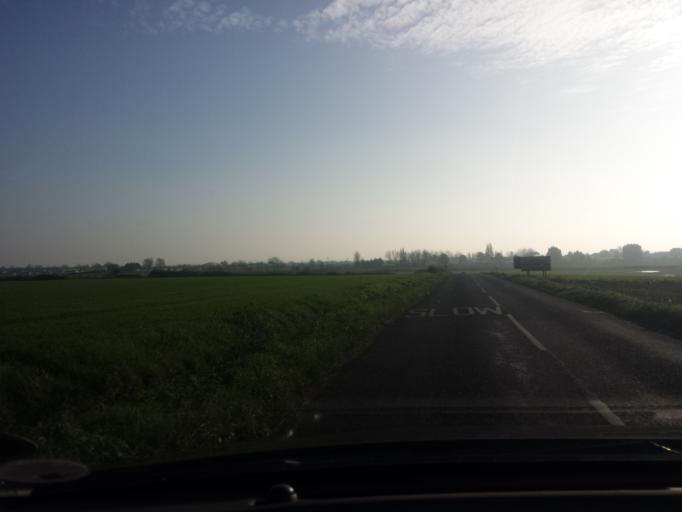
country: GB
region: England
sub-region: Essex
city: Saint Osyth
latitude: 51.7839
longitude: 1.0865
